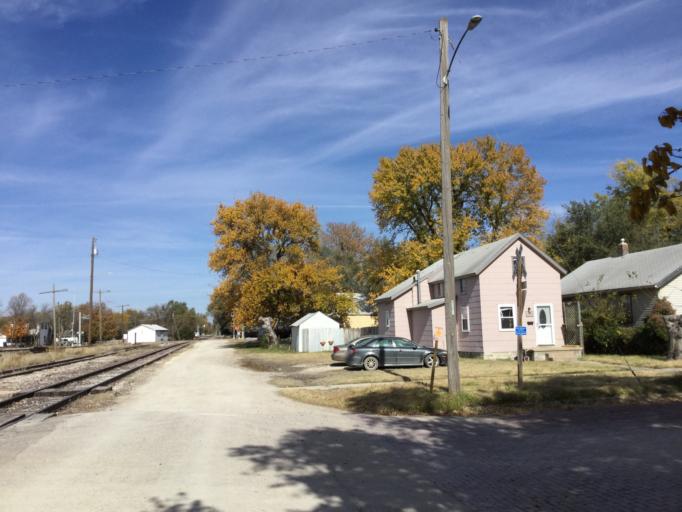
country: US
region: Kansas
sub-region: Harvey County
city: Newton
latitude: 38.0486
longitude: -97.3366
